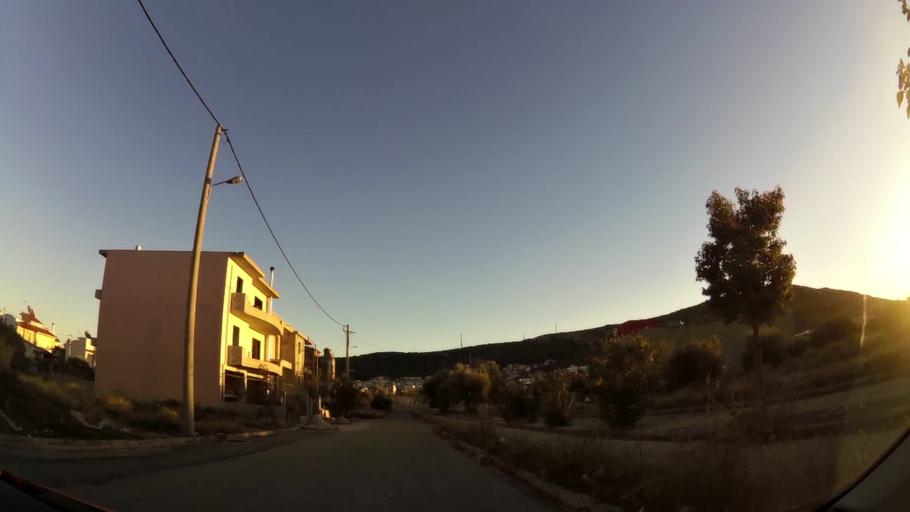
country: GR
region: Attica
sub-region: Nomarchia Dytikis Attikis
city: Ano Liosia
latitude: 38.0740
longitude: 23.6952
